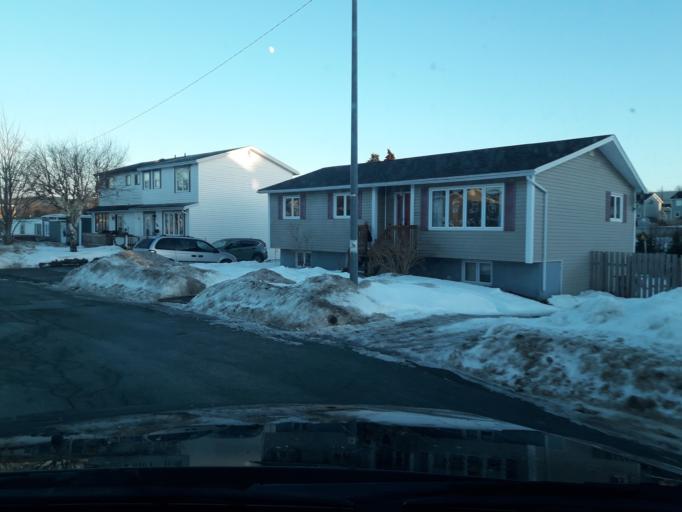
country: CA
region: Newfoundland and Labrador
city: Mount Pearl
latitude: 47.5229
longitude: -52.7692
